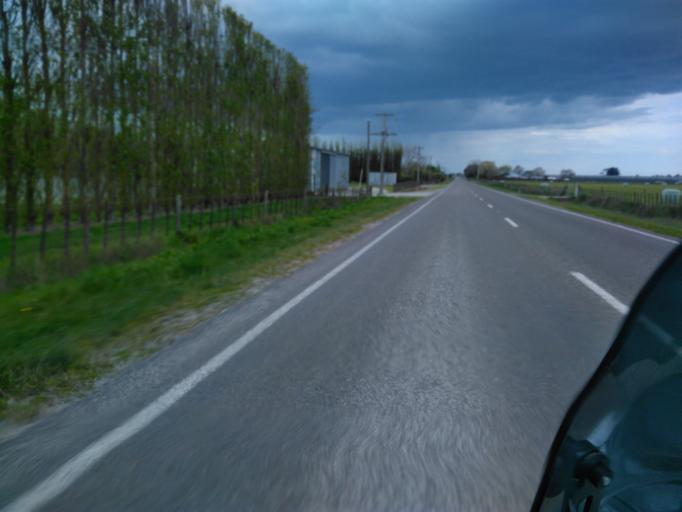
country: NZ
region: Gisborne
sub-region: Gisborne District
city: Gisborne
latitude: -38.6457
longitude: 177.9041
